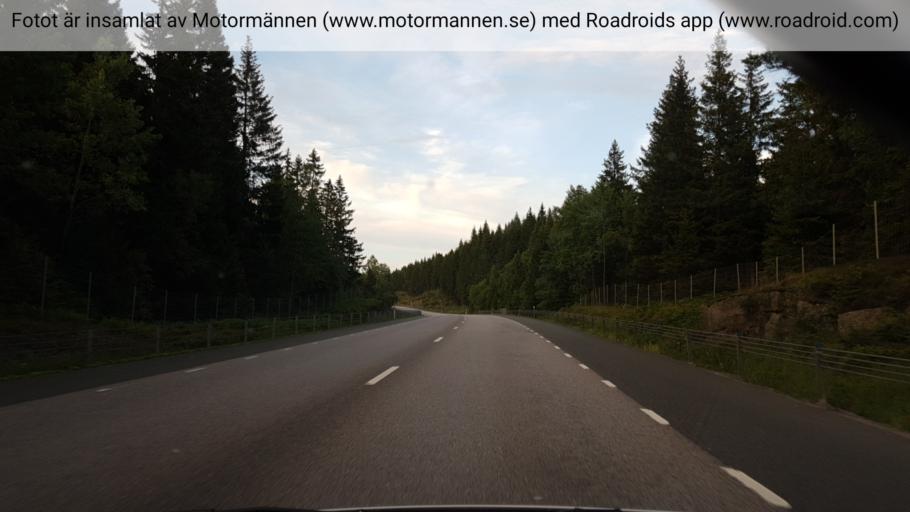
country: SE
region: Vaestra Goetaland
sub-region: Skovde Kommun
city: Skultorp
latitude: 58.3859
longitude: 13.7402
